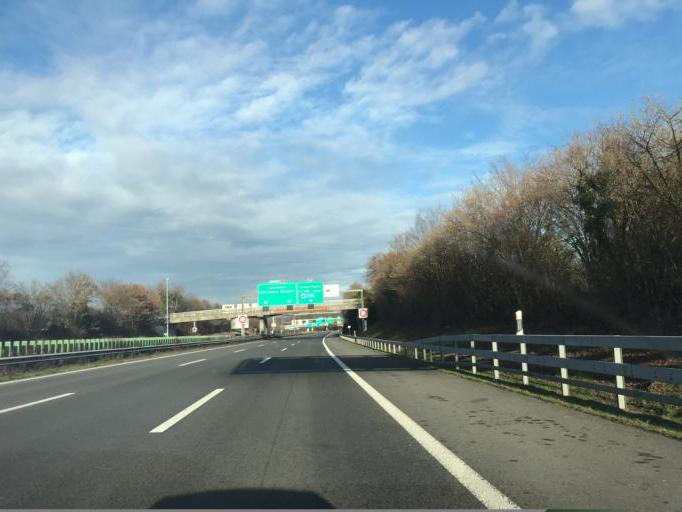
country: FR
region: Rhone-Alpes
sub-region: Departement de la Haute-Savoie
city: Saint-Julien-en-Genevois
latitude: 46.1520
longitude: 6.0973
